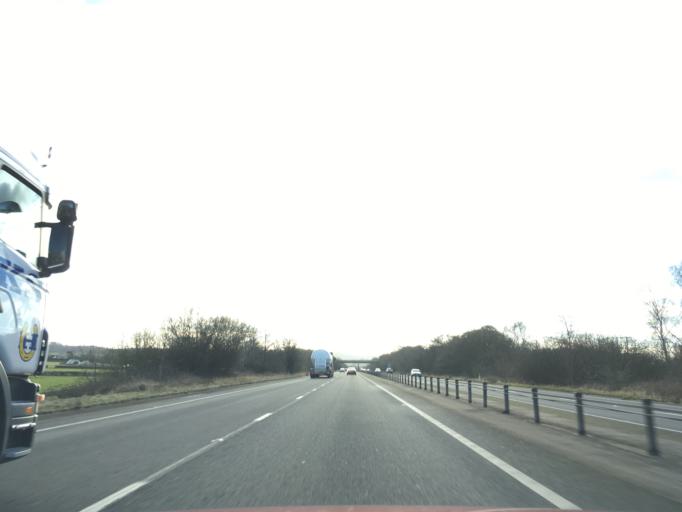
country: GB
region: Wales
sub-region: Monmouthshire
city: Llangwm
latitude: 51.7480
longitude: -2.8419
